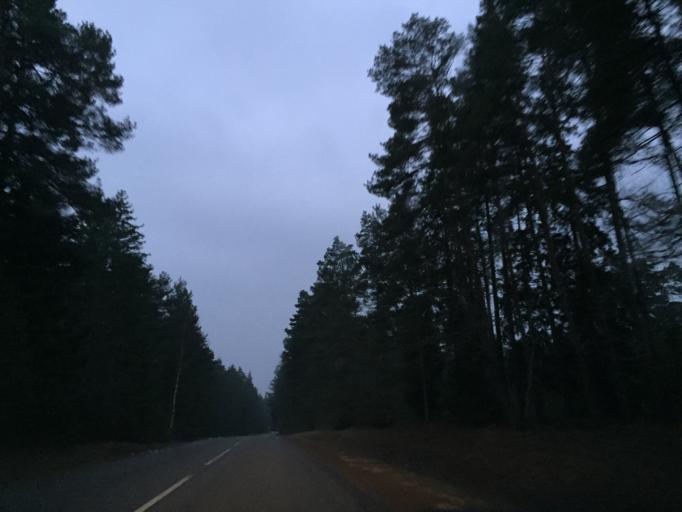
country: EE
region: Saare
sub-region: Kuressaare linn
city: Kuressaare
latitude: 58.5962
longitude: 22.6080
